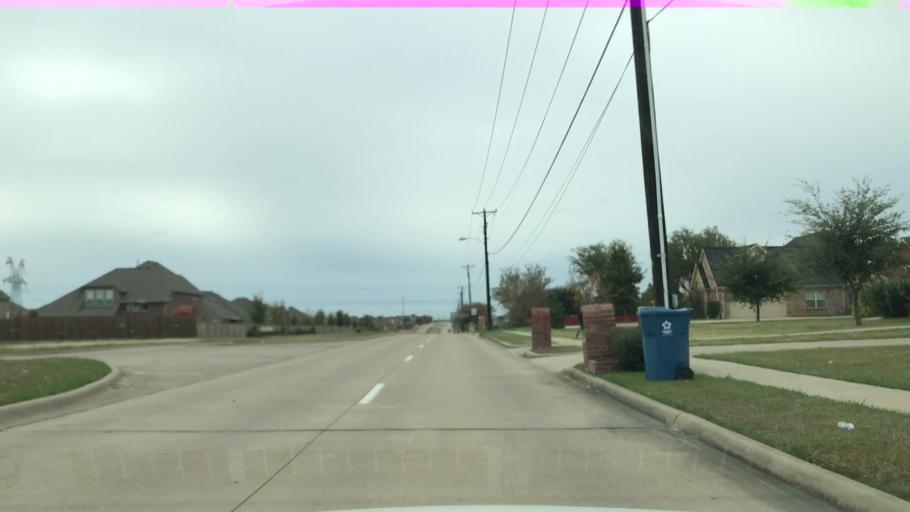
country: US
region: Texas
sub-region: Dallas County
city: Sachse
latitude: 32.9710
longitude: -96.5834
